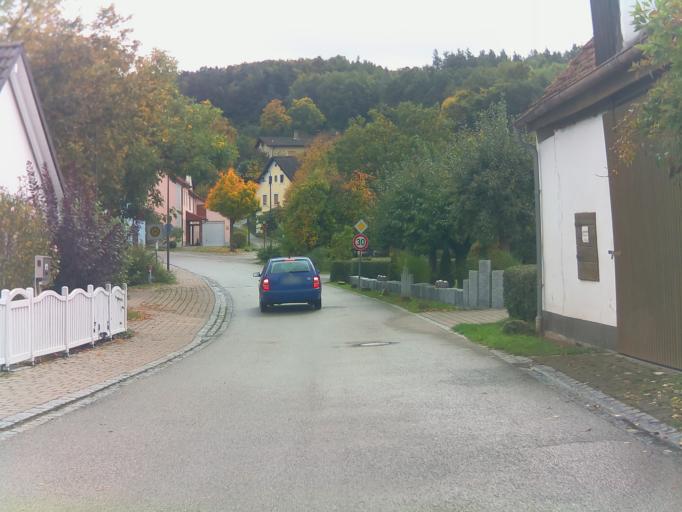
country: DE
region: Bavaria
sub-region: Upper Franconia
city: Priesendorf
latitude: 49.9210
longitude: 10.7423
